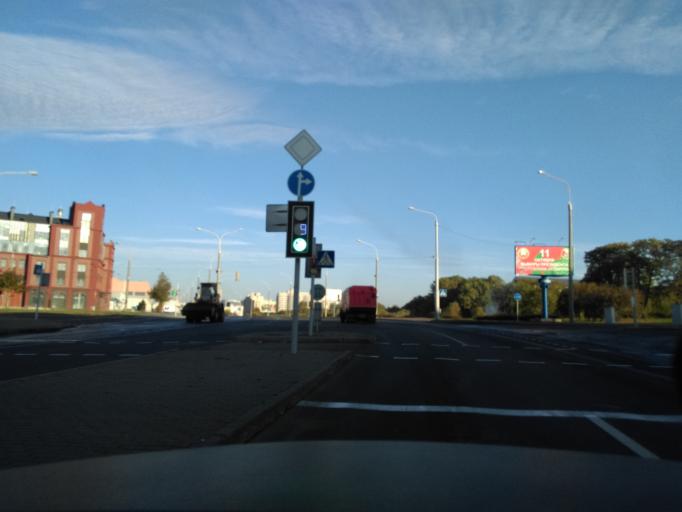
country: BY
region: Minsk
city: Minsk
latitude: 53.8888
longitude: 27.5794
